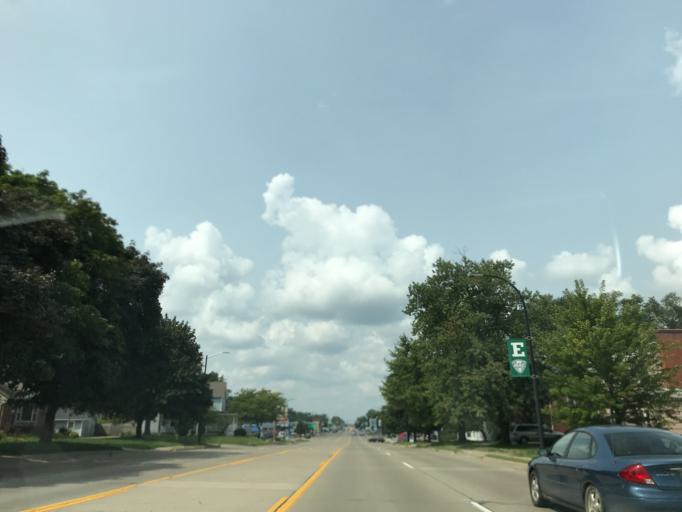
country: US
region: Michigan
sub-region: Washtenaw County
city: Ypsilanti
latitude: 42.2468
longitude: -83.6330
